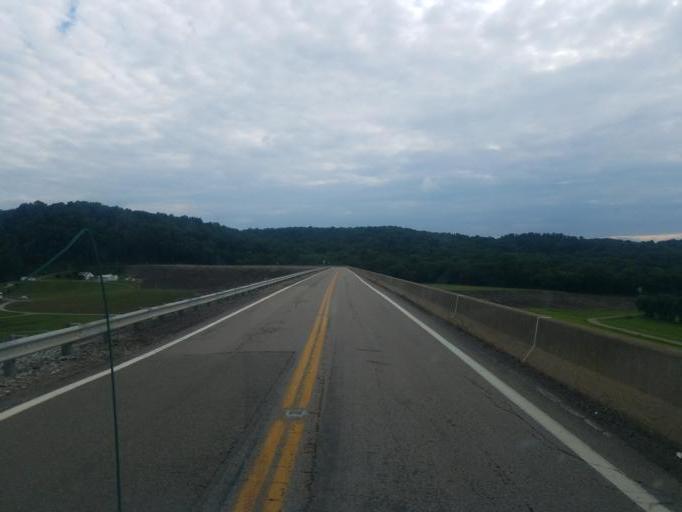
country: US
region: Ohio
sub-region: Knox County
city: Oak Hill
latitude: 40.3526
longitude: -82.0866
